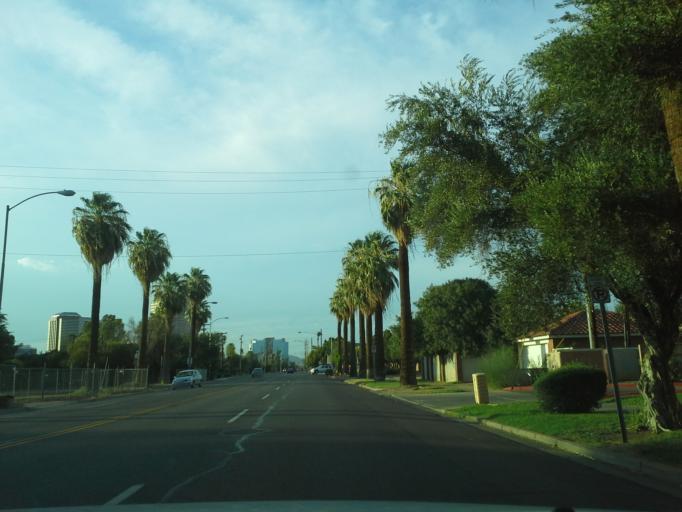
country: US
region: Arizona
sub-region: Maricopa County
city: Phoenix
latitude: 33.4717
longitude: -112.0694
